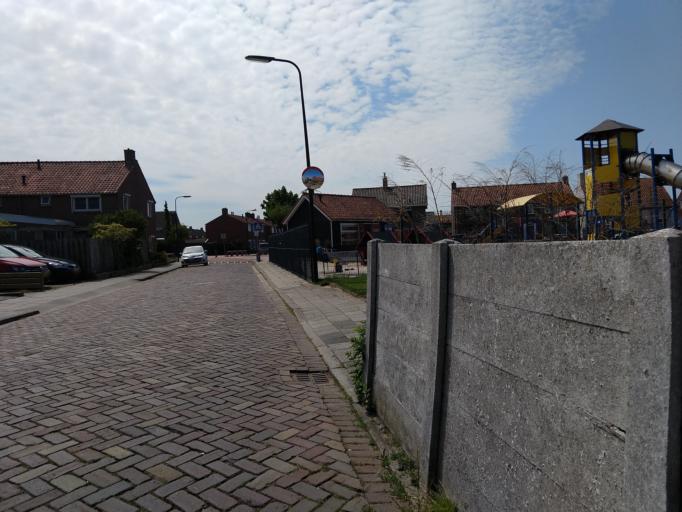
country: NL
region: Zeeland
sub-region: Schouwen-Duiveland
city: Bruinisse
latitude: 51.5992
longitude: 4.1017
